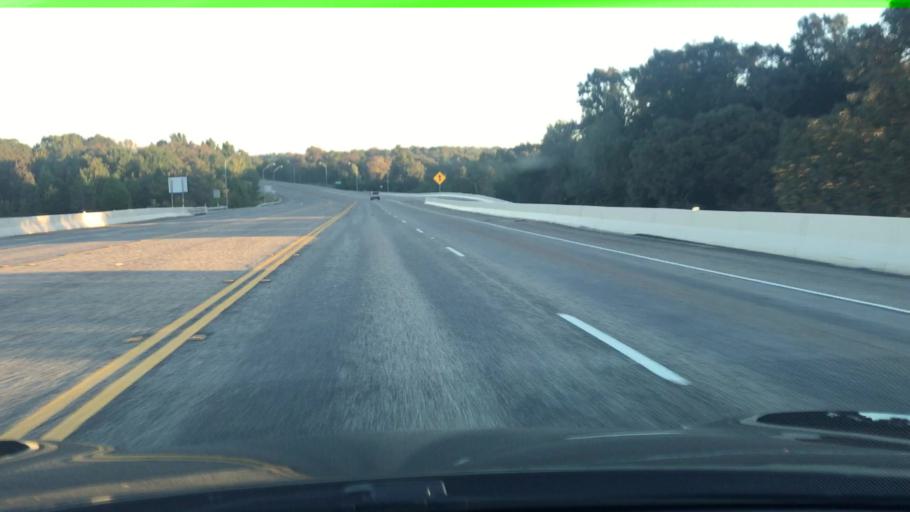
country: US
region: Texas
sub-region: Henderson County
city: Athens
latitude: 32.2097
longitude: -95.8050
